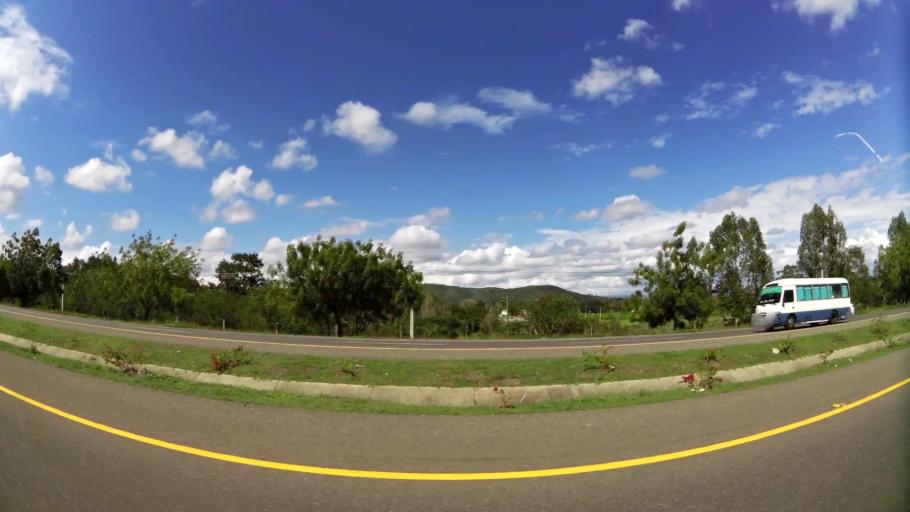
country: DO
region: La Vega
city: Concepcion de La Vega
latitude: 19.2493
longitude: -70.5524
